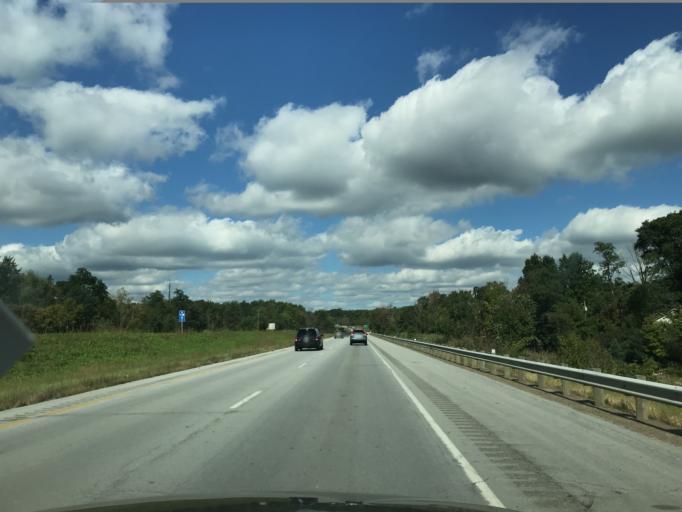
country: US
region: Ohio
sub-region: Summit County
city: Macedonia
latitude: 41.3294
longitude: -81.4769
